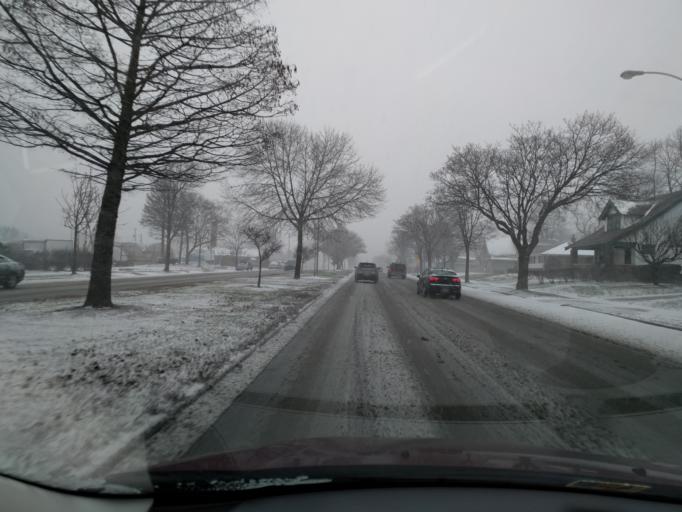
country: US
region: Wisconsin
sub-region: Milwaukee County
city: Brown Deer
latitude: 43.1193
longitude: -87.9832
